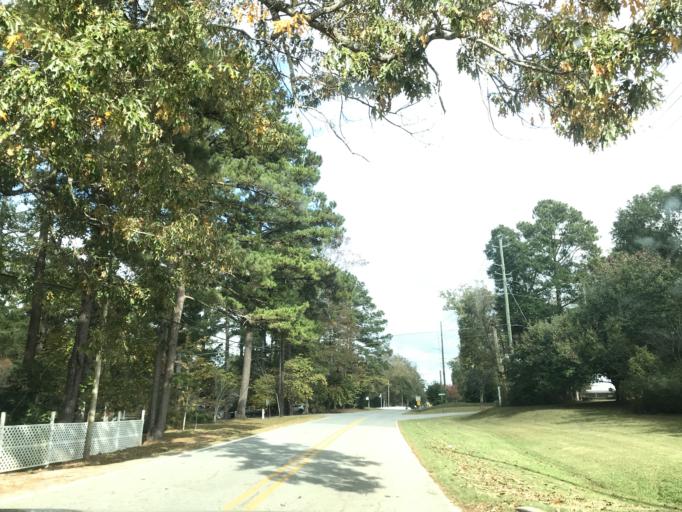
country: US
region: Georgia
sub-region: Jones County
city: Gray
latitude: 33.0055
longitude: -83.5493
